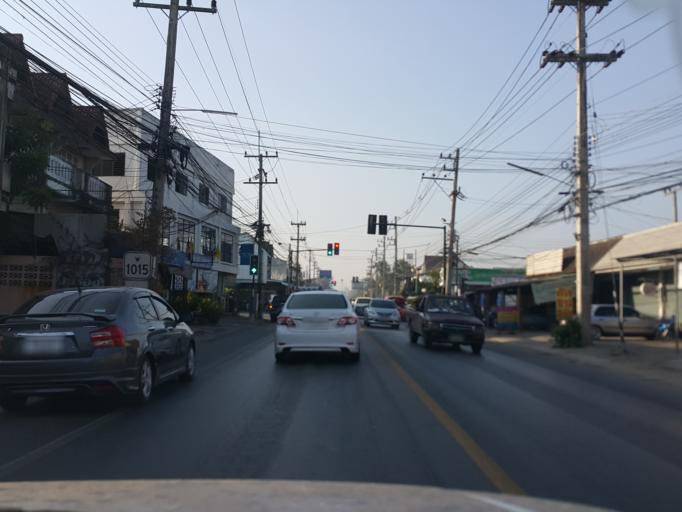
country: TH
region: Chiang Mai
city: San Pa Tong
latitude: 18.6324
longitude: 98.8977
